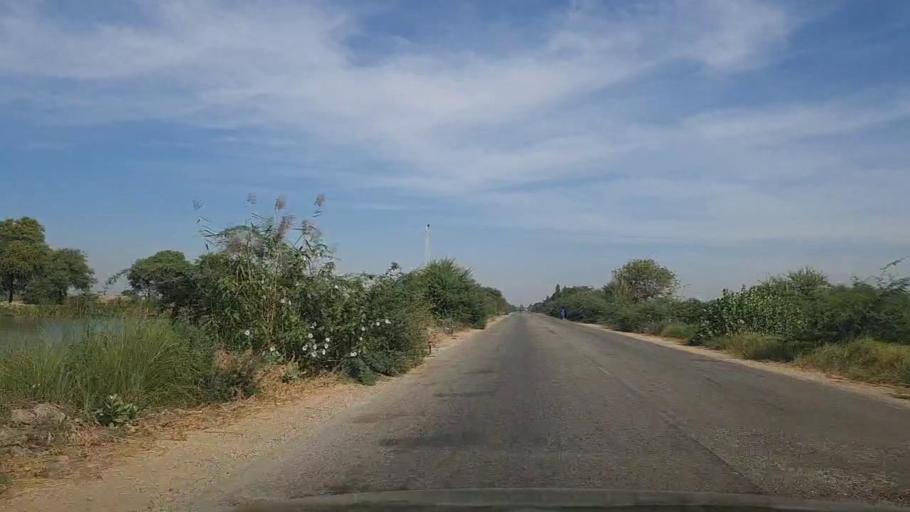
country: PK
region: Sindh
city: Daro Mehar
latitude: 24.9725
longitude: 68.1251
